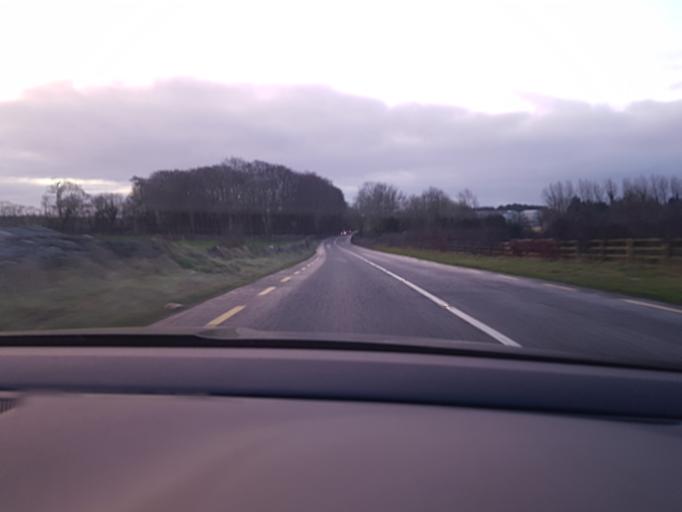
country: IE
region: Connaught
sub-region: County Galway
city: Tuam
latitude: 53.5333
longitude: -8.8785
